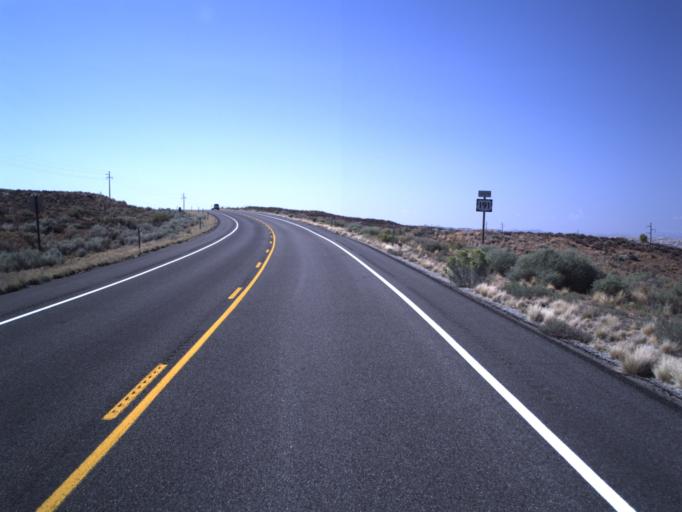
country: US
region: Utah
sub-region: San Juan County
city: Blanding
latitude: 37.3547
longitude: -109.5178
